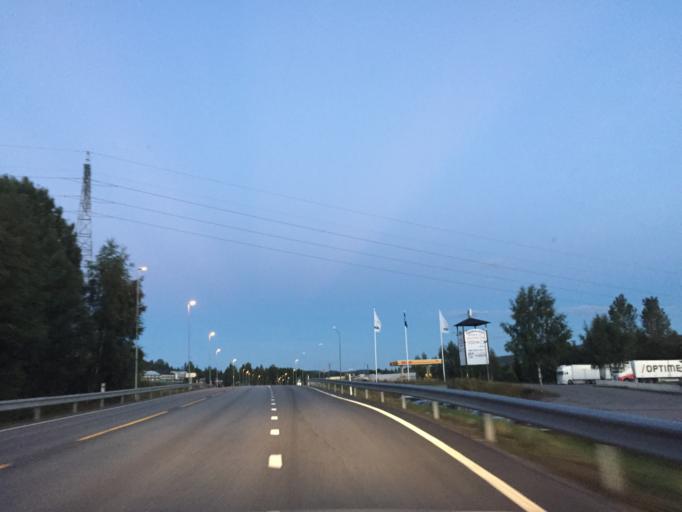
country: NO
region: Hedmark
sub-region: Kongsvinger
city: Kongsvinger
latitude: 60.2093
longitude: 11.9651
